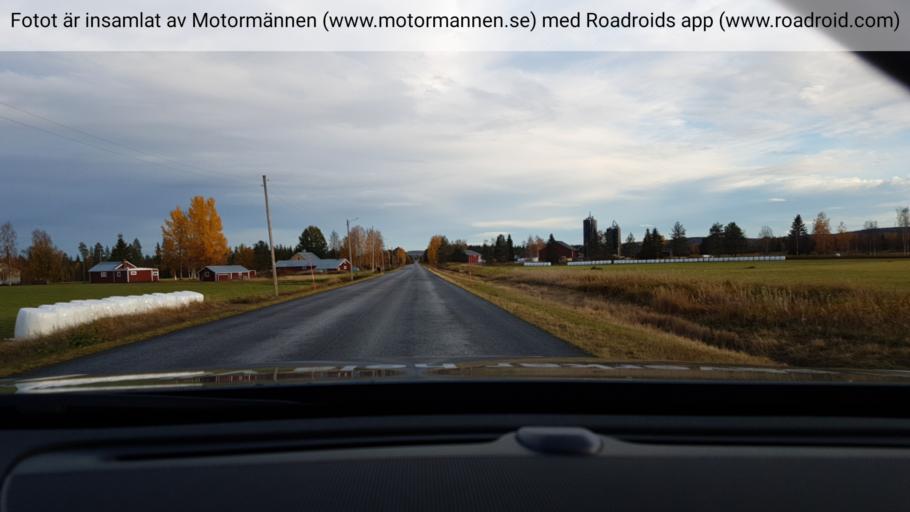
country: SE
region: Norrbotten
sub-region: Overkalix Kommun
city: OEverkalix
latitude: 66.9540
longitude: 22.7030
